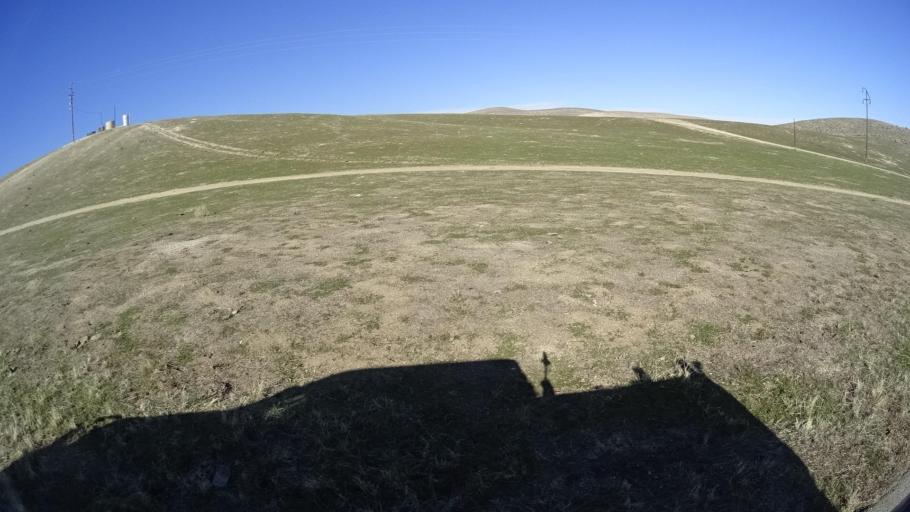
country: US
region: California
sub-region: Kern County
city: Taft Heights
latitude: 35.2322
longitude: -119.6624
